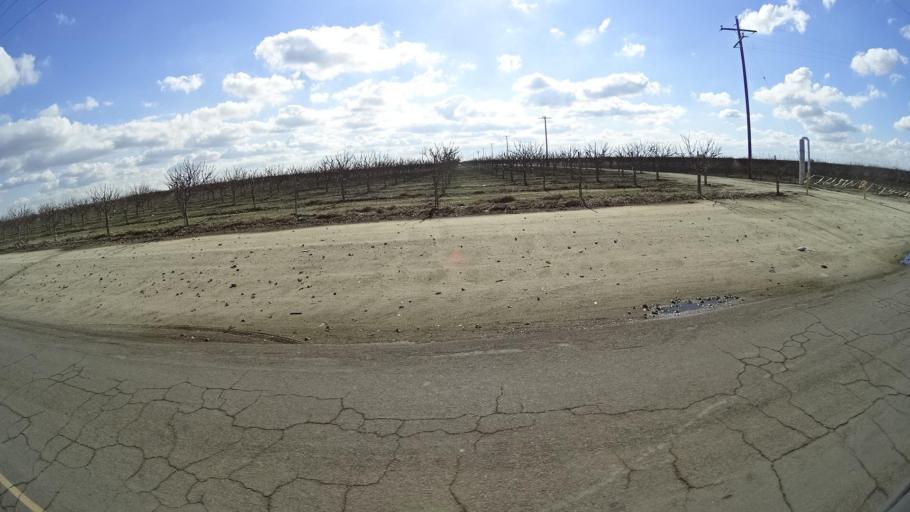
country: US
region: California
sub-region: Kern County
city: Delano
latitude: 35.7323
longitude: -119.2667
